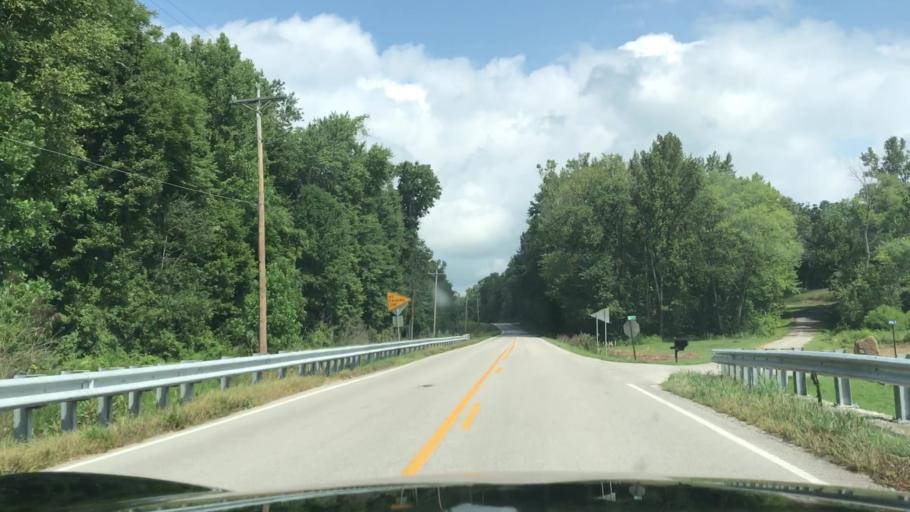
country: US
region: Kentucky
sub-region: Ohio County
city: Oak Grove
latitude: 37.1938
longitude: -86.8837
